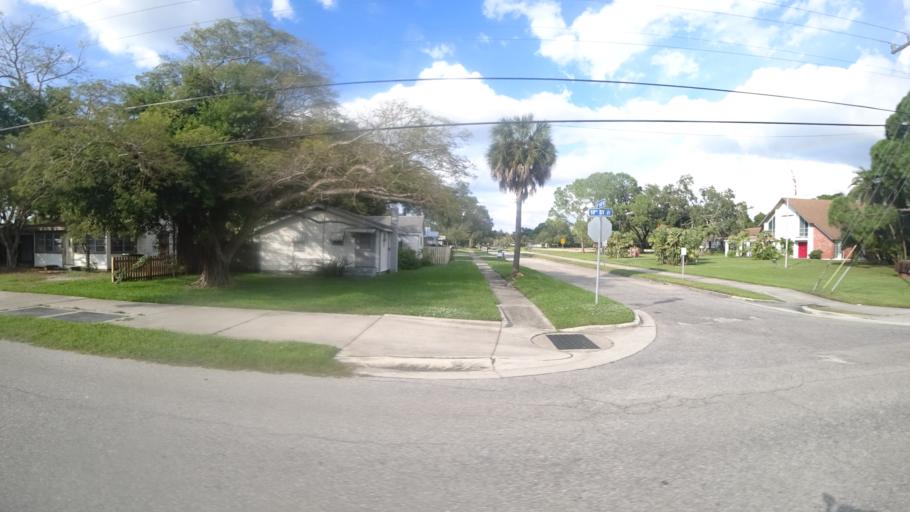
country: US
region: Florida
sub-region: Manatee County
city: Palmetto
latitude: 27.5213
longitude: -82.5936
